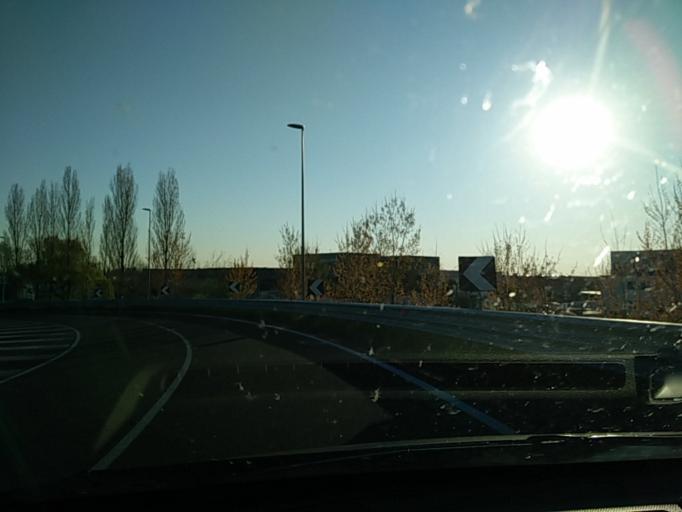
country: IT
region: Veneto
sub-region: Provincia di Venezia
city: Quarto d'Altino
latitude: 45.5810
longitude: 12.3543
